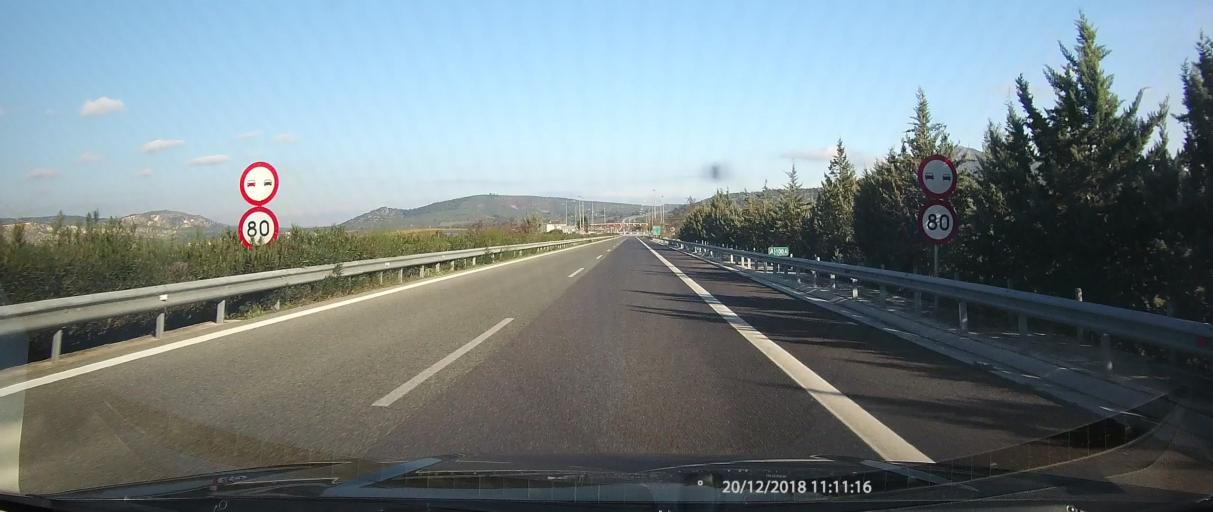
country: GR
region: Peloponnese
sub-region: Nomos Korinthias
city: Ayios Vasilios
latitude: 37.8307
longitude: 22.8045
